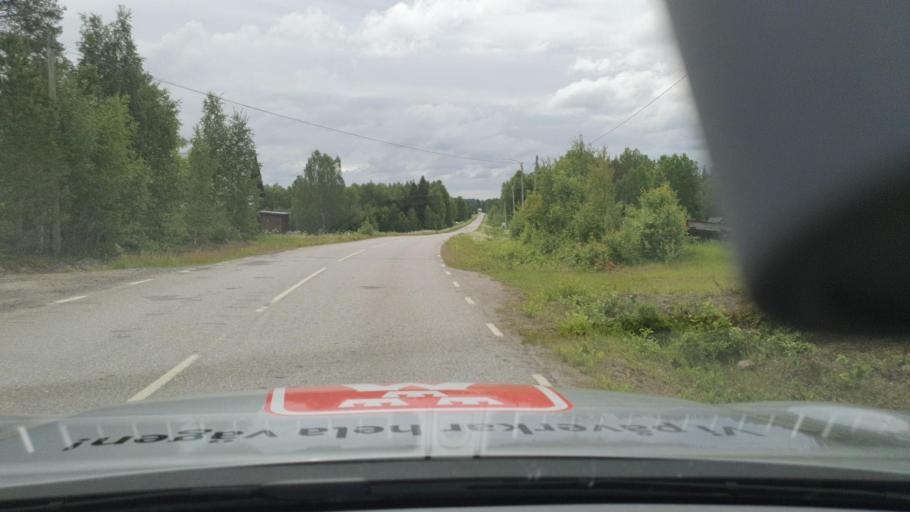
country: SE
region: Norrbotten
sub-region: Lulea Kommun
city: Ranea
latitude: 65.9288
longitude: 22.1426
